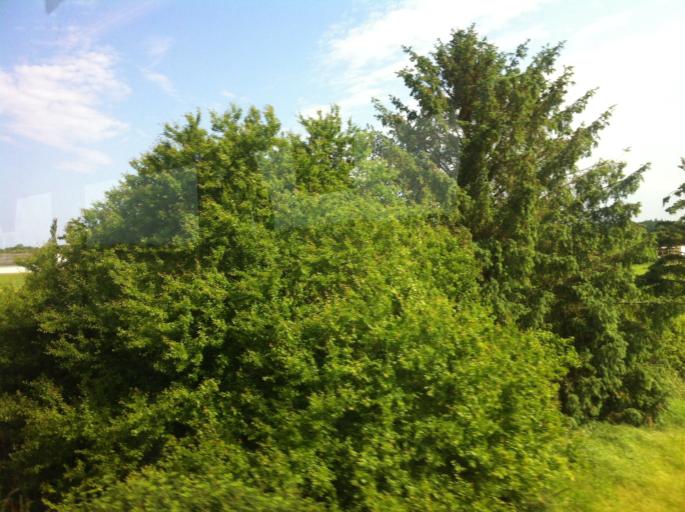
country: DK
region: Capital Region
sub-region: Helsingor Kommune
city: Hornbaek
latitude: 56.0787
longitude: 12.4771
